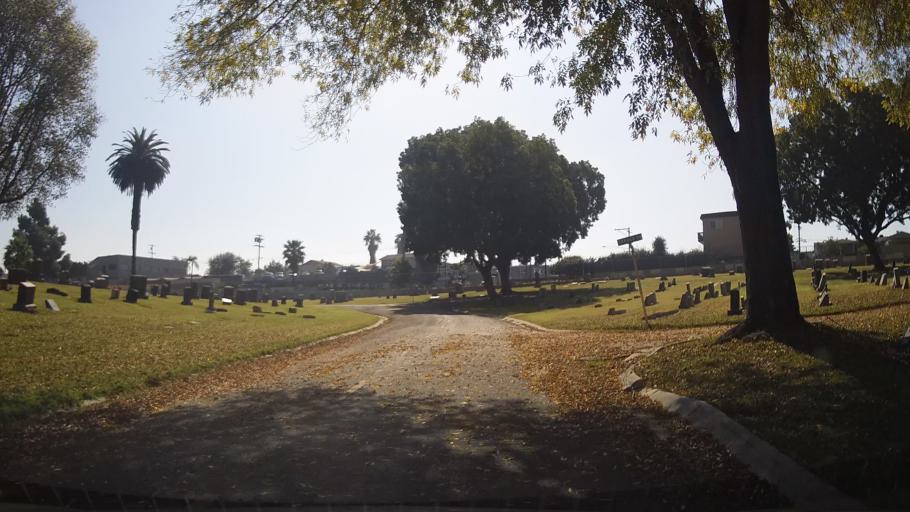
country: US
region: California
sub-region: San Diego County
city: National City
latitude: 32.7057
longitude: -117.1131
